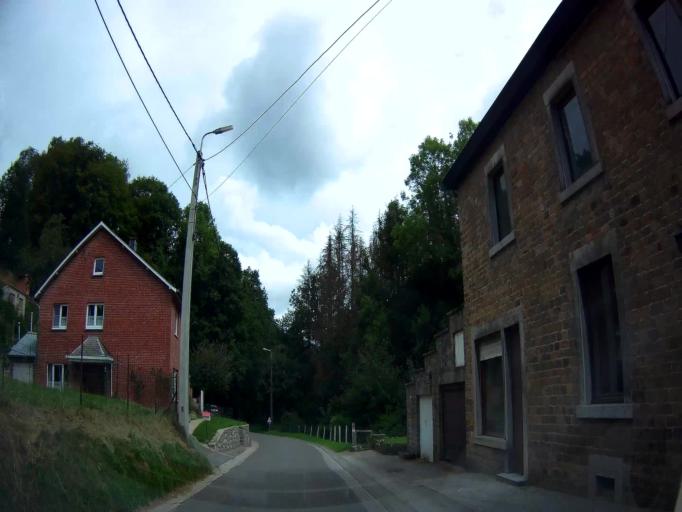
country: BE
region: Wallonia
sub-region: Province de Liege
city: Modave
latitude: 50.4475
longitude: 5.2711
